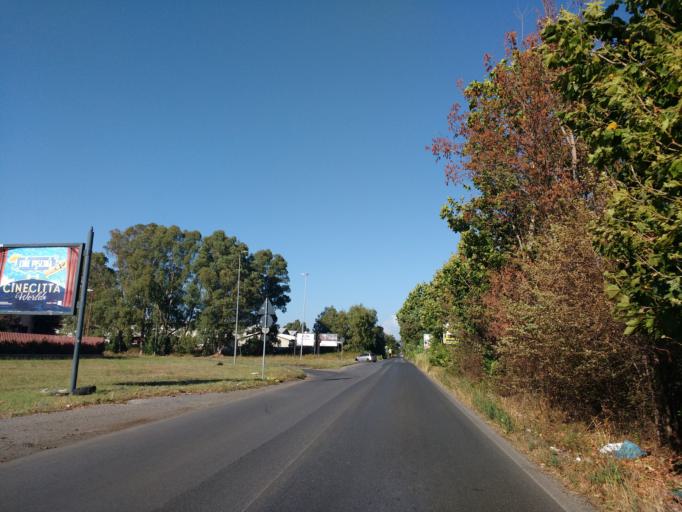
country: IT
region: Latium
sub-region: Citta metropolitana di Roma Capitale
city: Acilia-Castel Fusano-Ostia Antica
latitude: 41.7689
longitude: 12.3217
